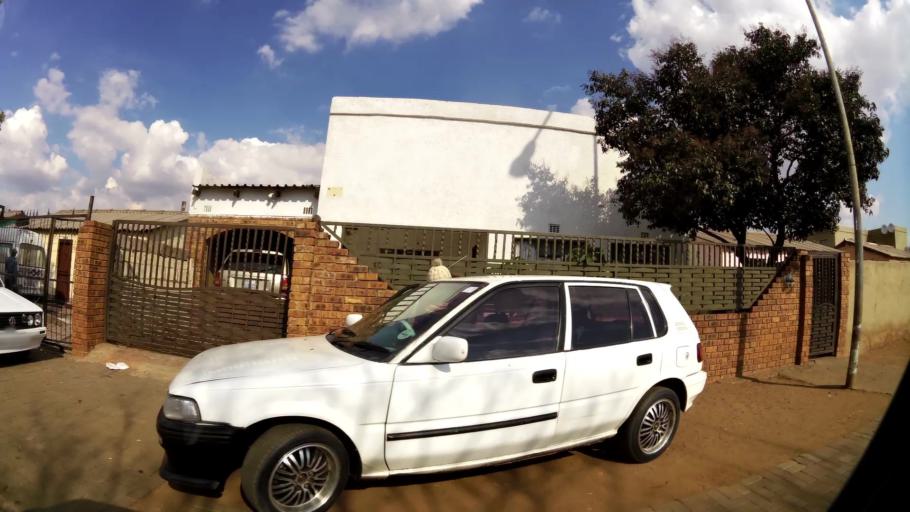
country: ZA
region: Gauteng
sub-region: City of Johannesburg Metropolitan Municipality
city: Soweto
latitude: -26.2235
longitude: 27.8652
